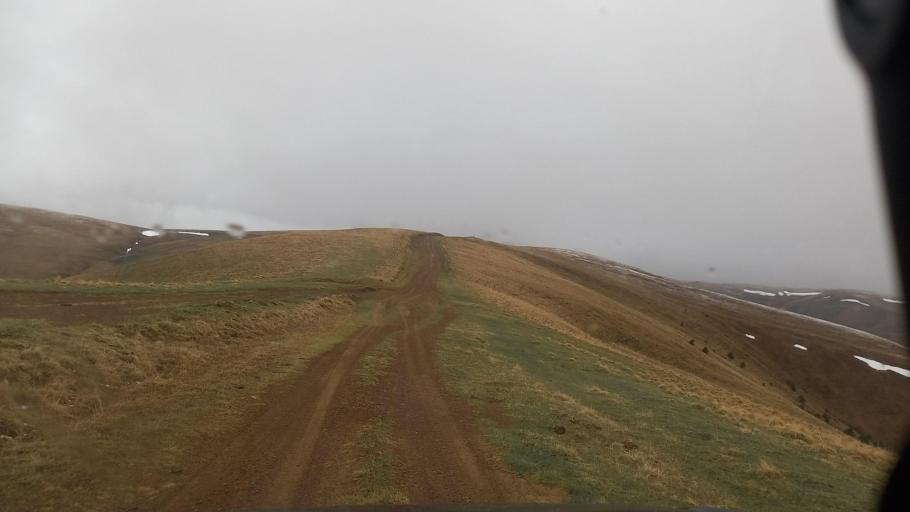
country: RU
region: Karachayevo-Cherkesiya
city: Uchkeken
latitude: 43.5983
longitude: 42.5023
